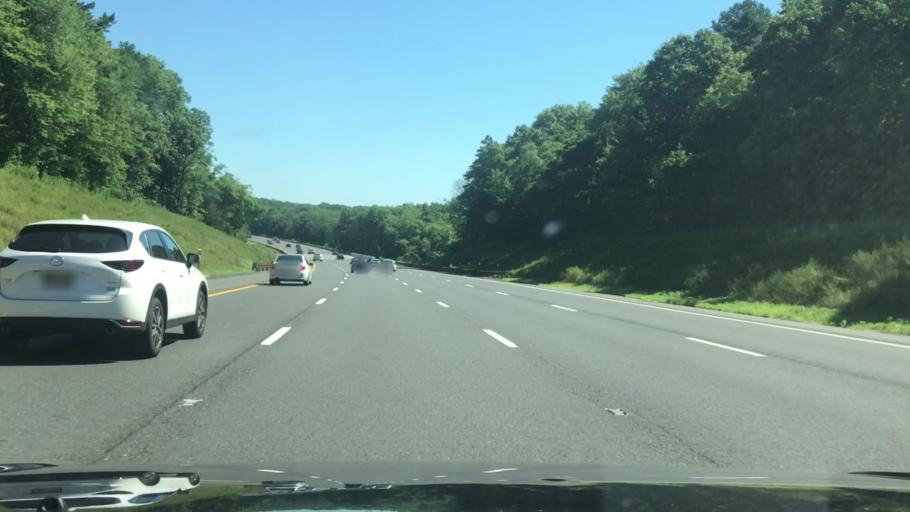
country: US
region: New Jersey
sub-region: Monmouth County
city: Ramtown
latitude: 40.1360
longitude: -74.1150
